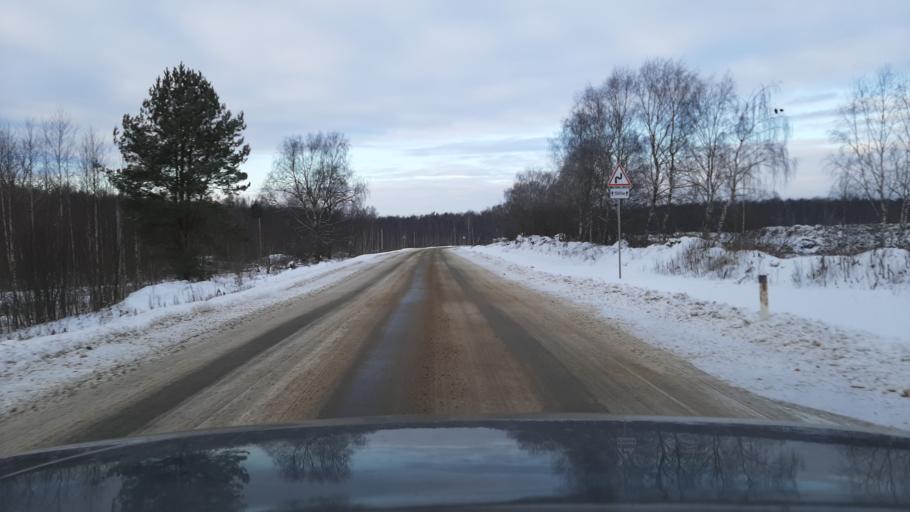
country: RU
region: Kostroma
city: Nerekhta
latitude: 57.4687
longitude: 40.6281
